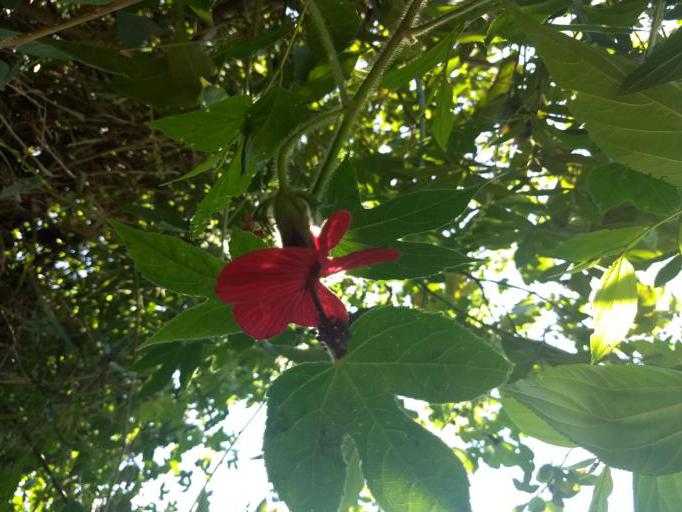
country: MX
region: Puebla
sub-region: Cuetzalan del Progreso
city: Ciudad de Cuetzalan
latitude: 20.0105
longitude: -97.5067
